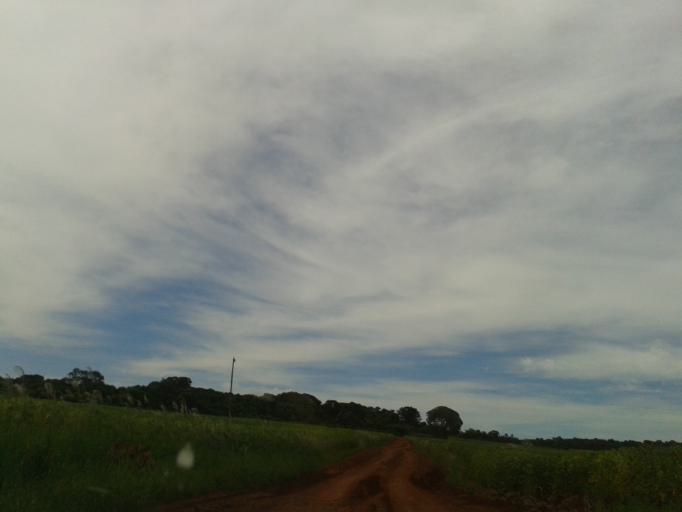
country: BR
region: Minas Gerais
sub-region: Capinopolis
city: Capinopolis
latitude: -18.7673
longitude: -49.8087
